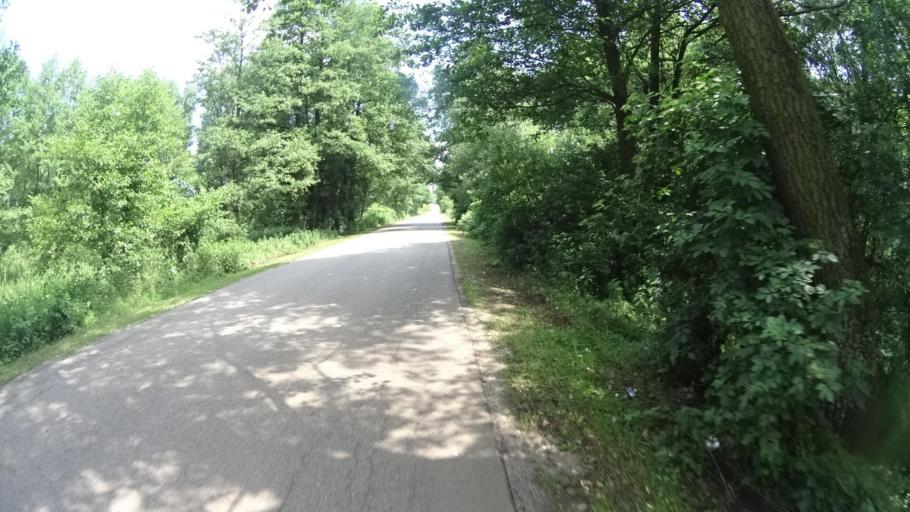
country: PL
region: Masovian Voivodeship
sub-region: Powiat bialobrzeski
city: Wysmierzyce
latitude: 51.6628
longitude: 20.8414
